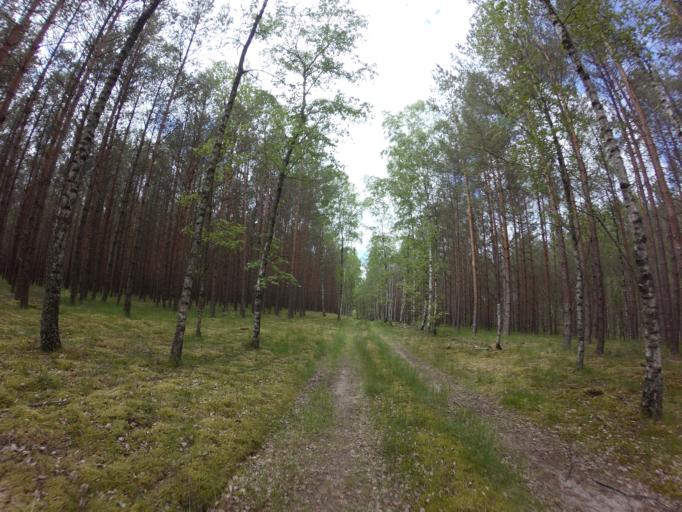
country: PL
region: West Pomeranian Voivodeship
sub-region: Powiat drawski
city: Kalisz Pomorski
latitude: 53.1535
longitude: 15.9691
